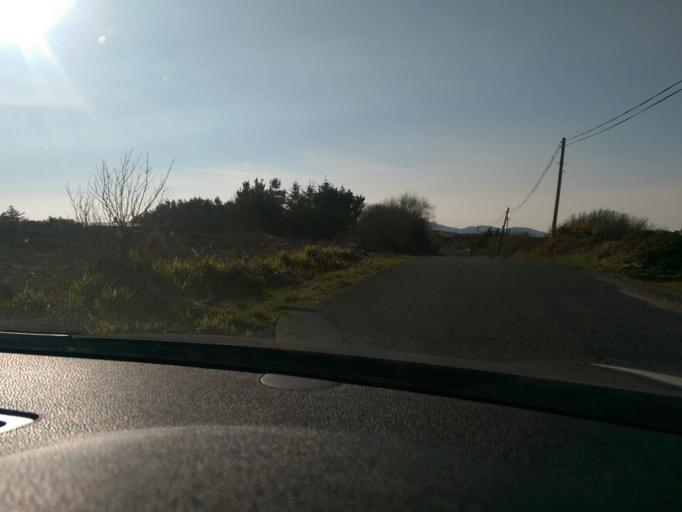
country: IE
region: Connaught
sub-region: County Galway
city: Clifden
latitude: 53.3737
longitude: -9.8290
